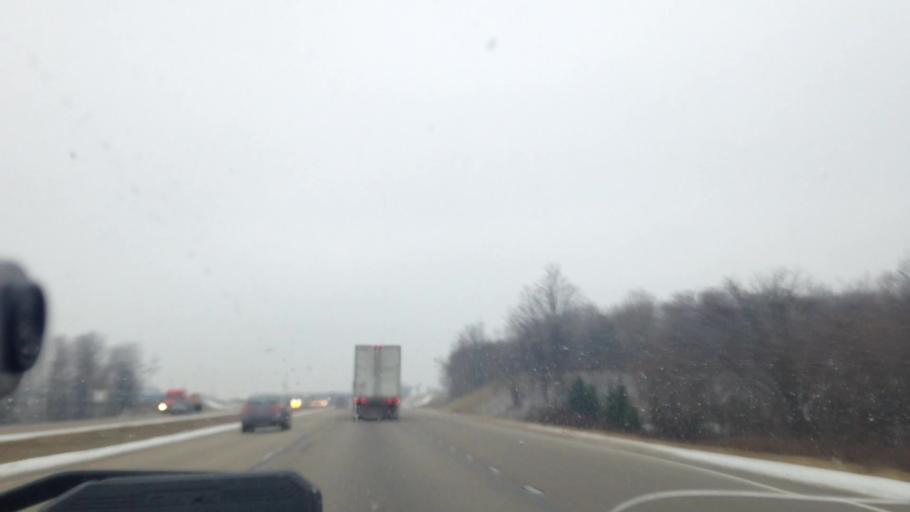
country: US
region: Wisconsin
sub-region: Washington County
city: Slinger
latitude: 43.3529
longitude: -88.2869
